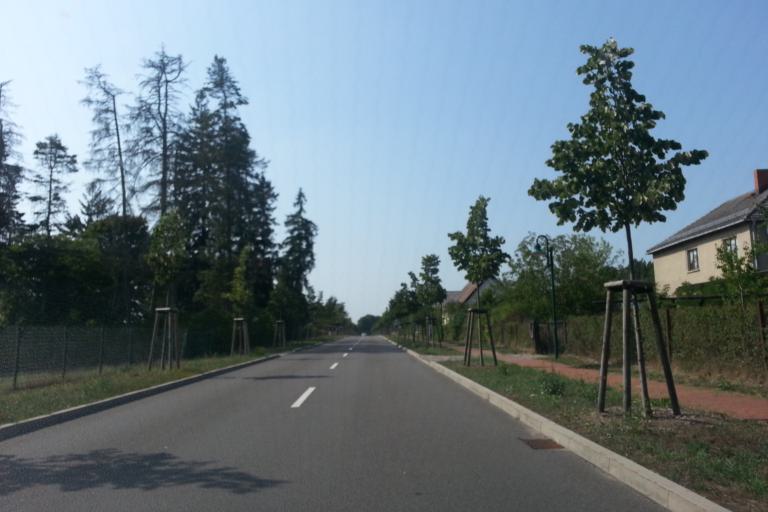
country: DE
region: Mecklenburg-Vorpommern
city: Strasburg
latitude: 53.6064
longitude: 13.7929
